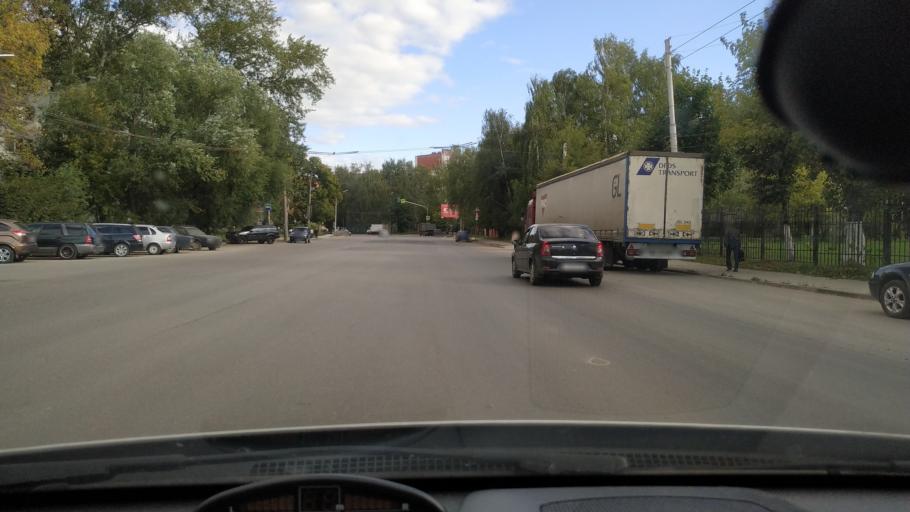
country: RU
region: Rjazan
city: Ryazan'
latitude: 54.6068
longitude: 39.7035
